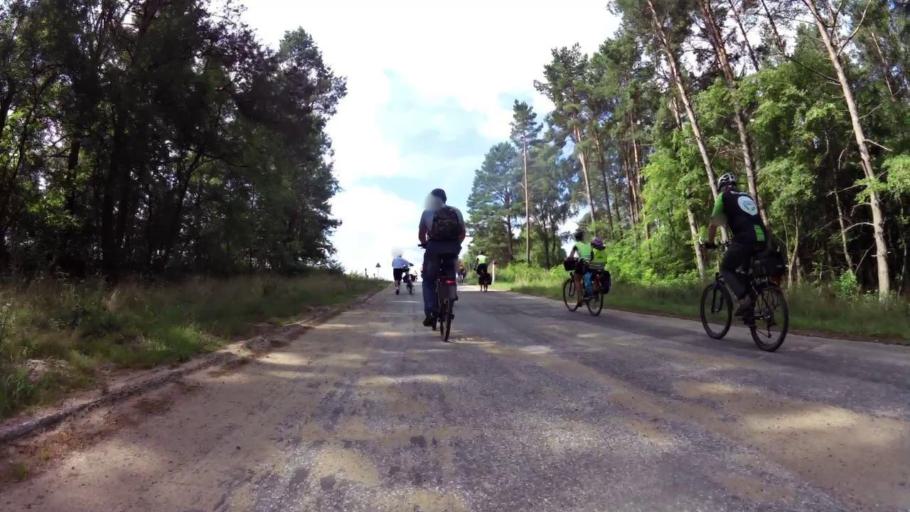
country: PL
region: West Pomeranian Voivodeship
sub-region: Powiat drawski
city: Drawsko Pomorskie
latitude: 53.4574
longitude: 15.7771
